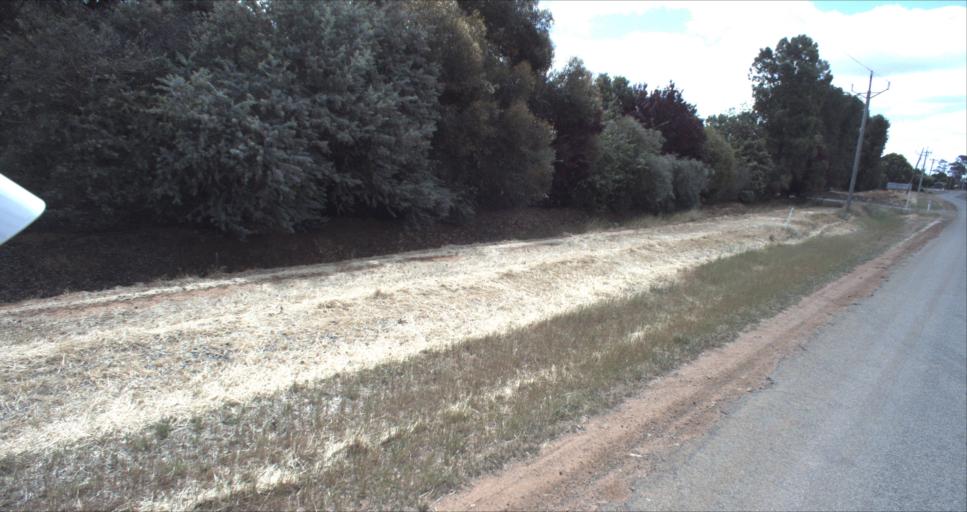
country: AU
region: New South Wales
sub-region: Leeton
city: Leeton
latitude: -34.5828
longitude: 146.3966
